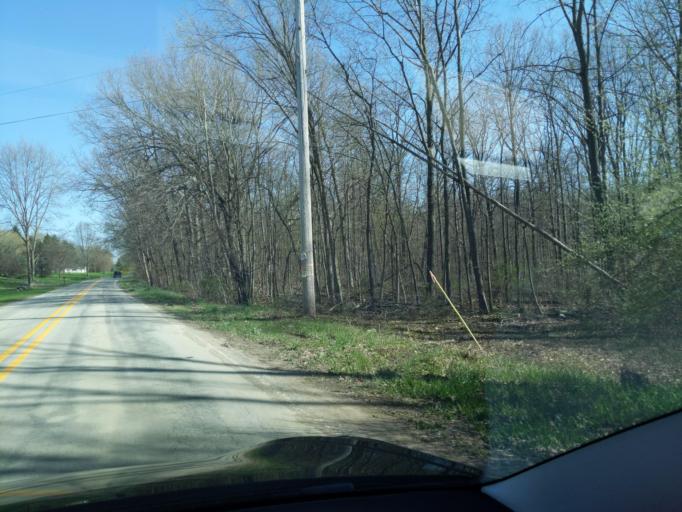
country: US
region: Michigan
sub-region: Ingham County
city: Stockbridge
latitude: 42.4460
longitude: -84.1029
